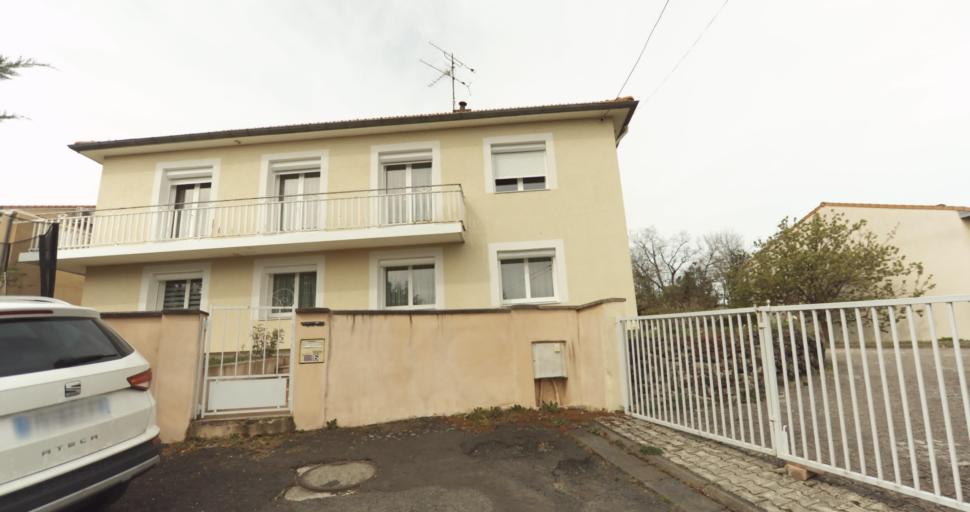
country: FR
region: Auvergne
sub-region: Departement du Puy-de-Dome
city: Cebazat
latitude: 45.8255
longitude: 3.0989
